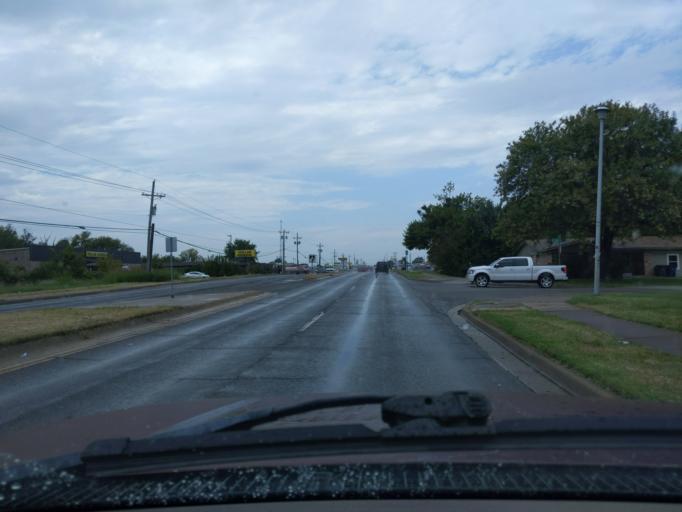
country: US
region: Oklahoma
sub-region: Tulsa County
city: Broken Arrow
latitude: 36.1336
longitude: -95.8430
